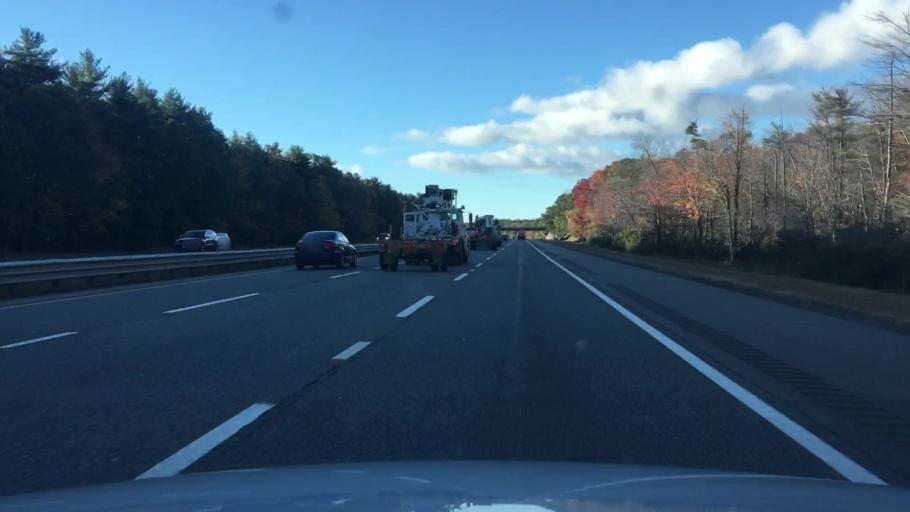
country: US
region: Maine
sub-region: York County
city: Cape Neddick
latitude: 43.2095
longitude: -70.6419
